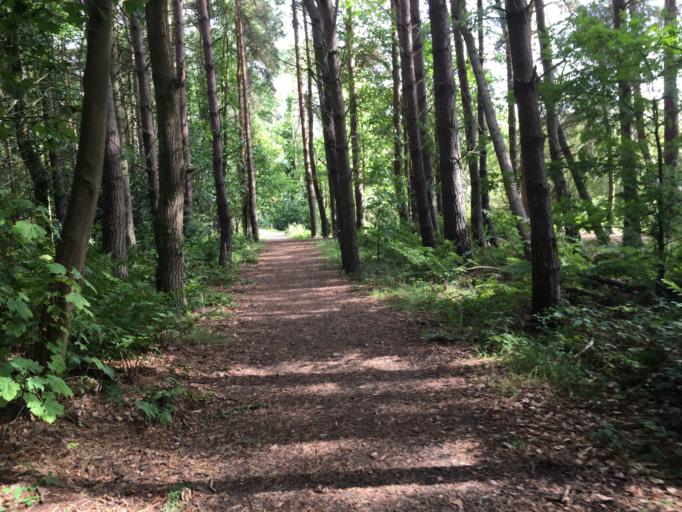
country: GB
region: Scotland
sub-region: Falkirk
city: Bo'ness
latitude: 56.0049
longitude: -3.6442
